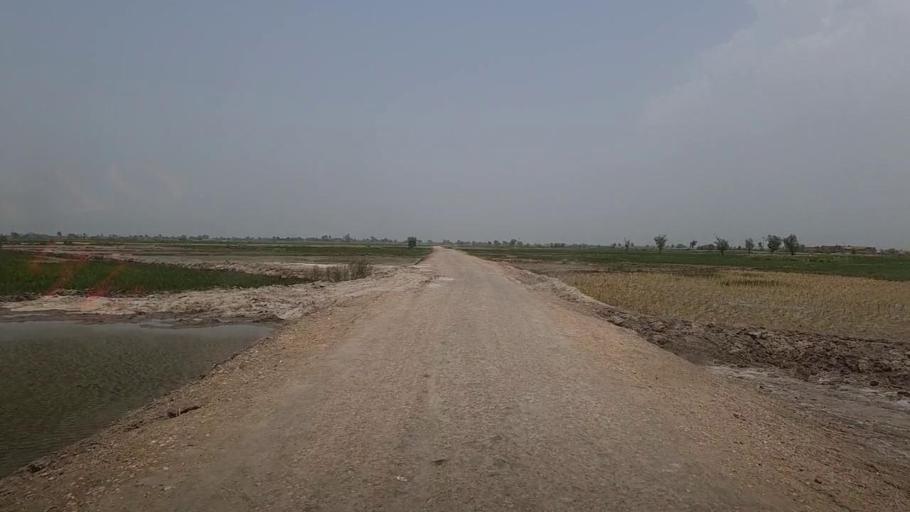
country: PK
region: Sindh
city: Sita Road
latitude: 27.0692
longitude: 67.8640
